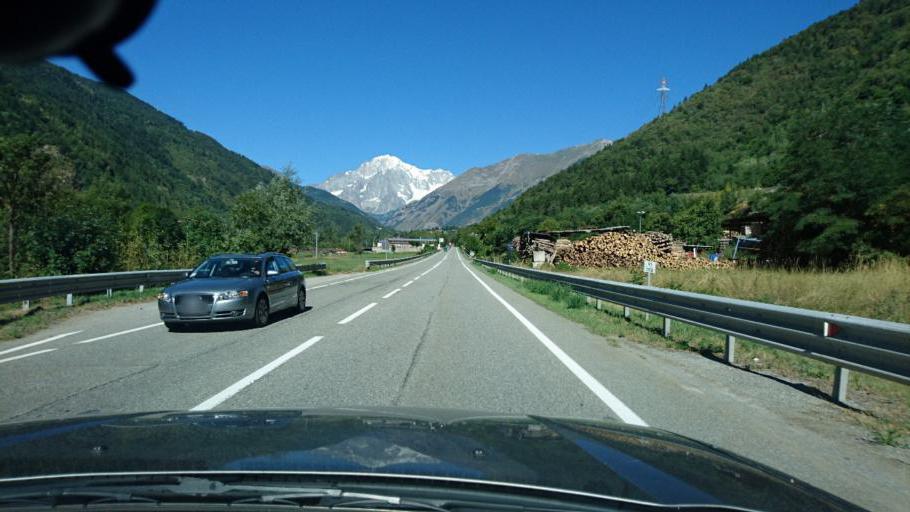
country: IT
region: Aosta Valley
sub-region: Valle d'Aosta
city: La Salle
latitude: 45.7224
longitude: 7.1000
